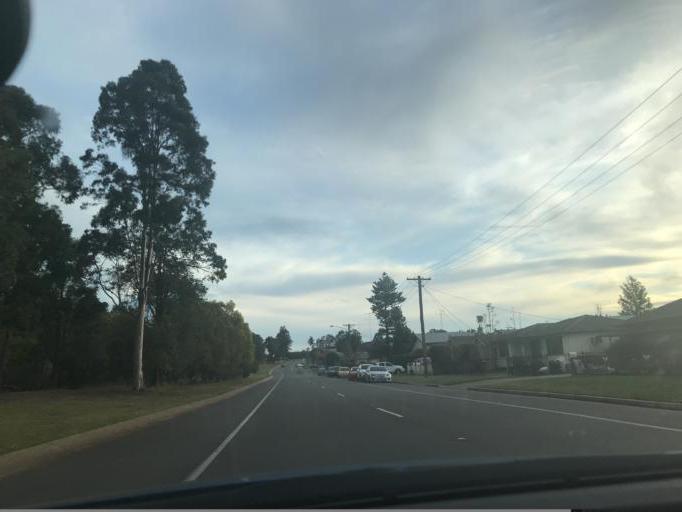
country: AU
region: New South Wales
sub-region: Cessnock
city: Cessnock
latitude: -32.8602
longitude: 151.3202
